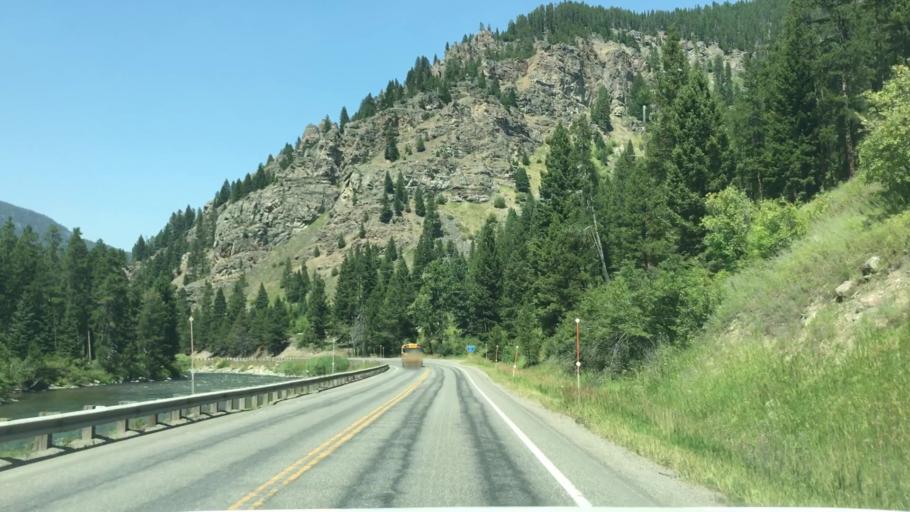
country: US
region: Montana
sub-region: Gallatin County
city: Big Sky
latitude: 45.3935
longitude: -111.2058
